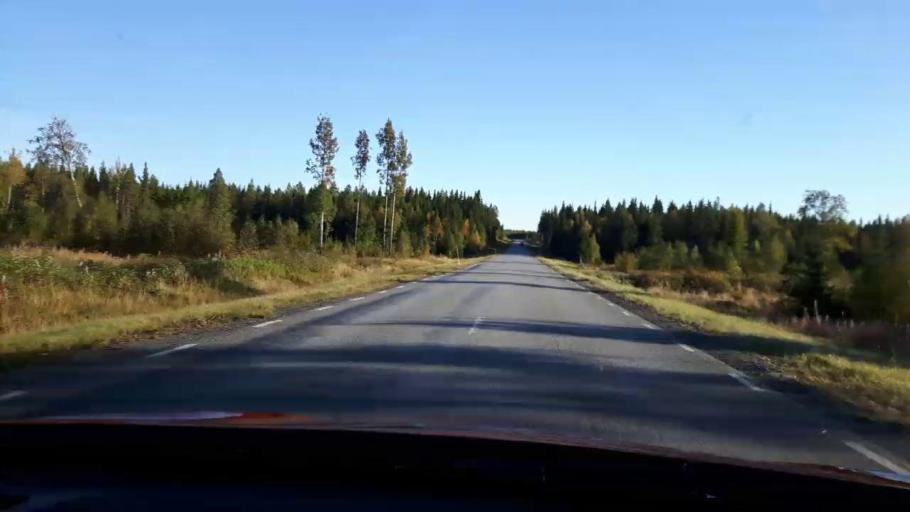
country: SE
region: Jaemtland
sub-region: OEstersunds Kommun
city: Lit
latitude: 63.7872
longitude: 14.7044
